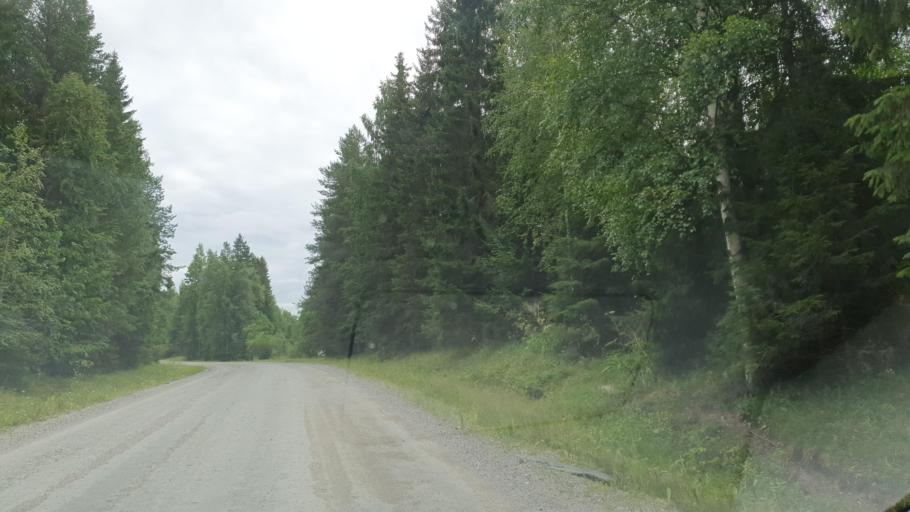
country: FI
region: Northern Savo
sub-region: Ylae-Savo
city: Iisalmi
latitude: 63.5389
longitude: 27.0736
